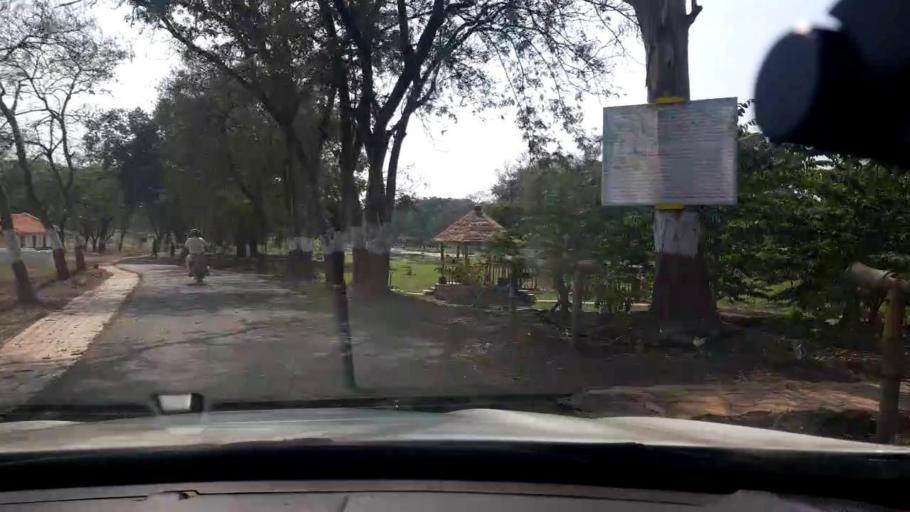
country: IN
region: Maharashtra
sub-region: Pune Division
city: Shivaji Nagar
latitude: 18.5443
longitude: 73.8559
